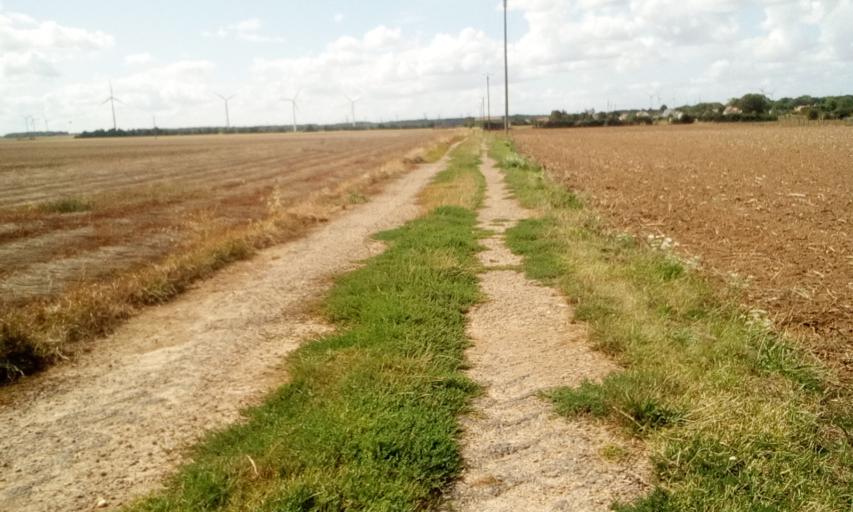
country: FR
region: Lower Normandy
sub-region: Departement du Calvados
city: Bellengreville
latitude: 49.1066
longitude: -0.2108
